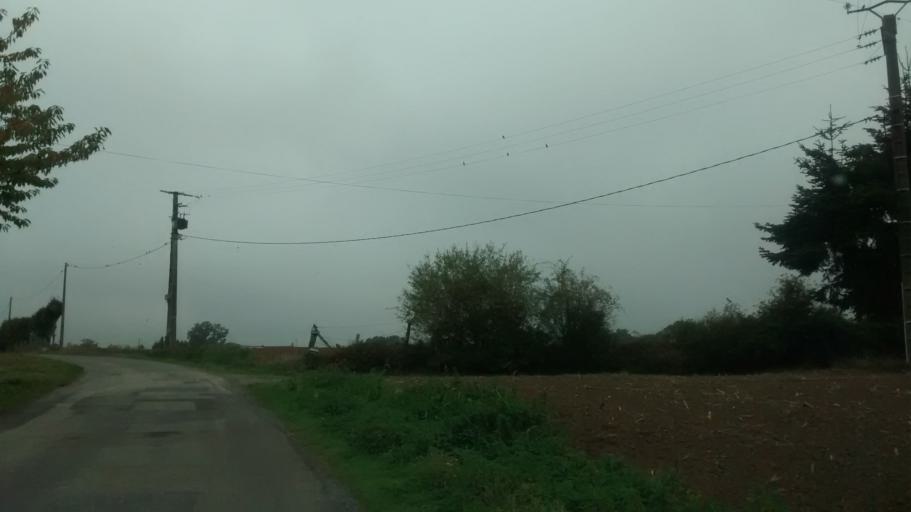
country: FR
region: Brittany
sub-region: Departement d'Ille-et-Vilaine
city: Cintre
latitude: 48.1141
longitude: -1.8982
